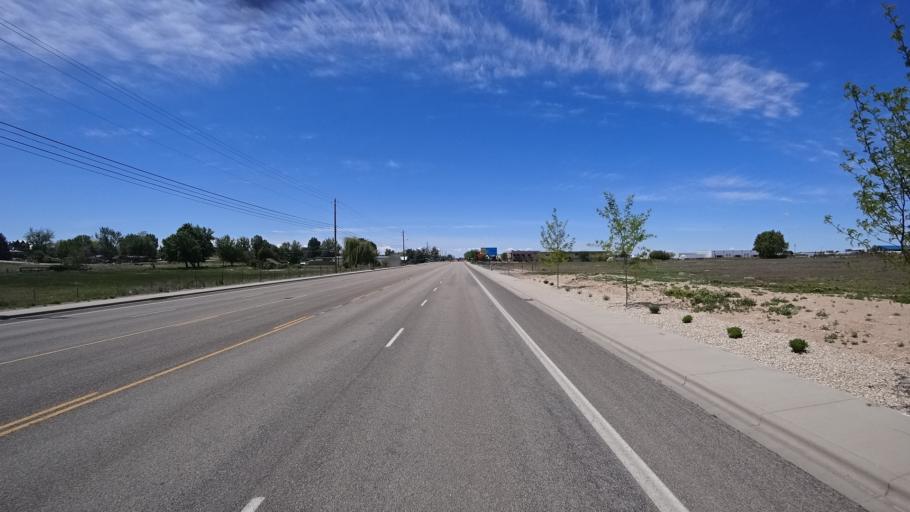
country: US
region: Idaho
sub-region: Ada County
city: Garden City
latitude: 43.5755
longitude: -116.2618
